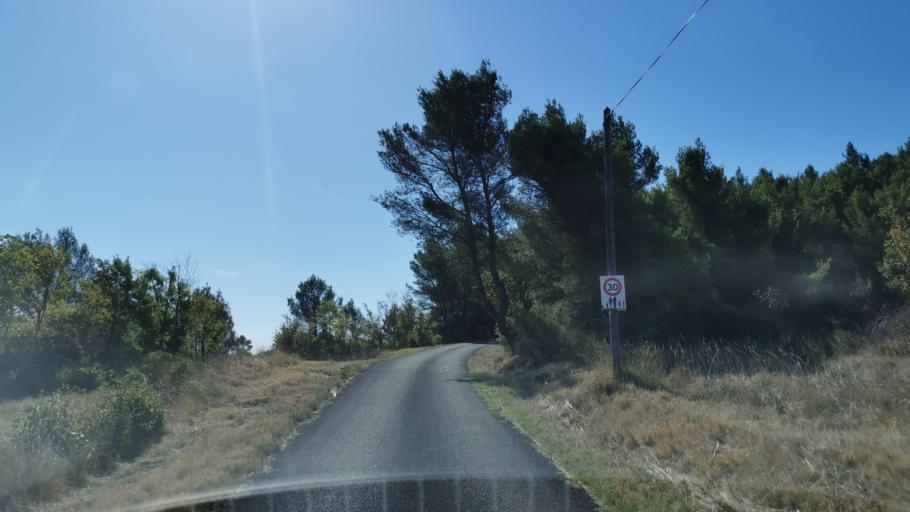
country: FR
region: Languedoc-Roussillon
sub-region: Departement de l'Aude
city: Conques-sur-Orbiel
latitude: 43.2471
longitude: 2.4101
